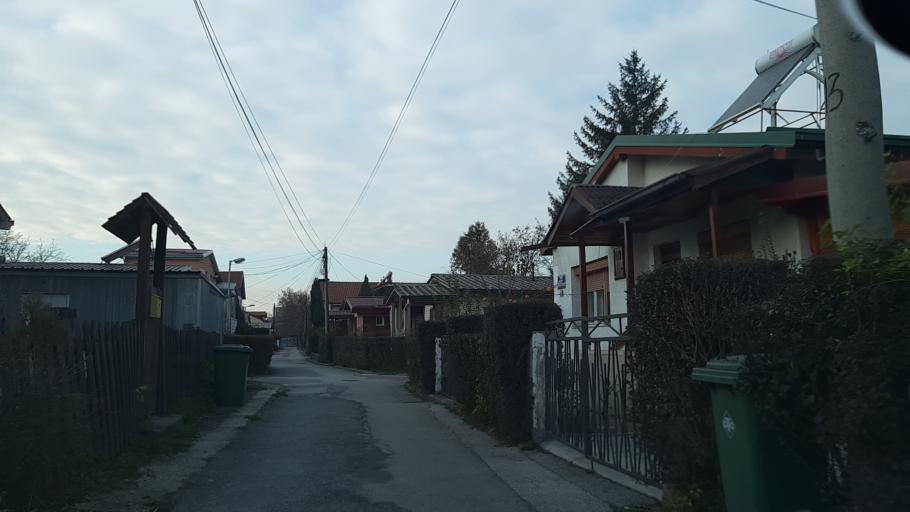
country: MK
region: Kisela Voda
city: Usje
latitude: 41.9764
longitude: 21.4523
